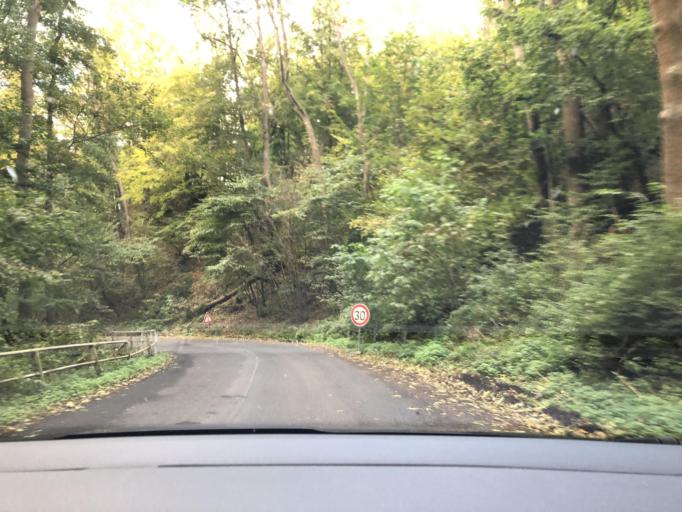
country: CZ
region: Ustecky
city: Velke Brezno
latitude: 50.6337
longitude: 14.1584
